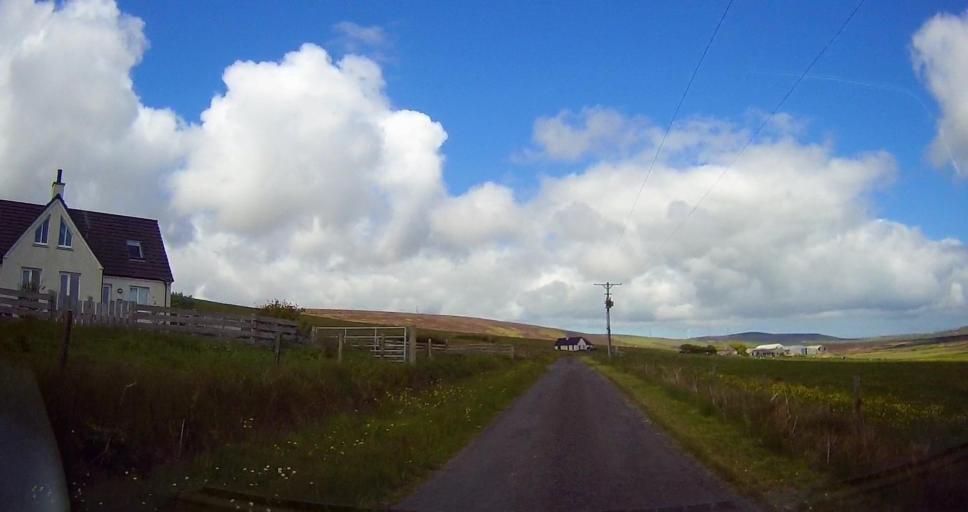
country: GB
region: Scotland
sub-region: Orkney Islands
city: Orkney
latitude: 59.0533
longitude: -3.1037
